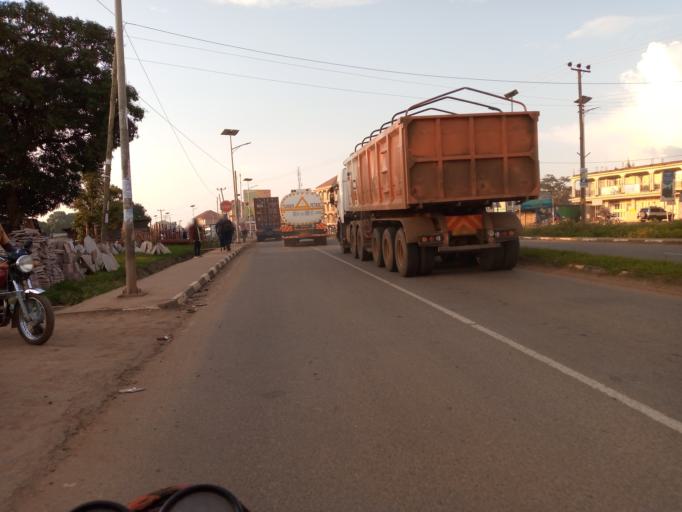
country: UG
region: Eastern Region
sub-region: Mbale District
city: Mbale
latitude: 1.0862
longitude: 34.1779
